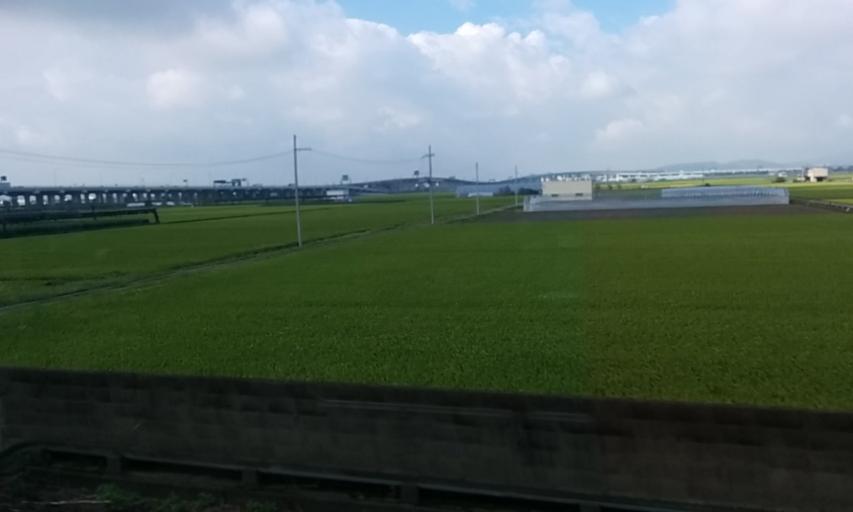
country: JP
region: Kyoto
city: Uji
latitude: 34.9107
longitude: 135.7727
